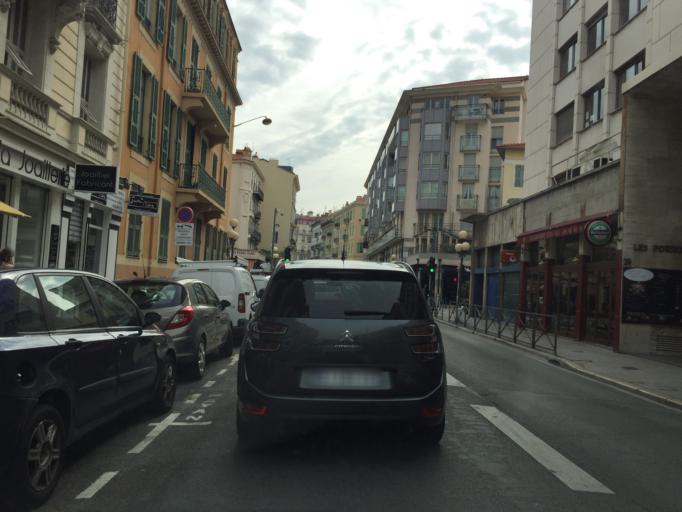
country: FR
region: Provence-Alpes-Cote d'Azur
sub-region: Departement des Alpes-Maritimes
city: Nice
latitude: 43.7006
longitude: 7.2707
